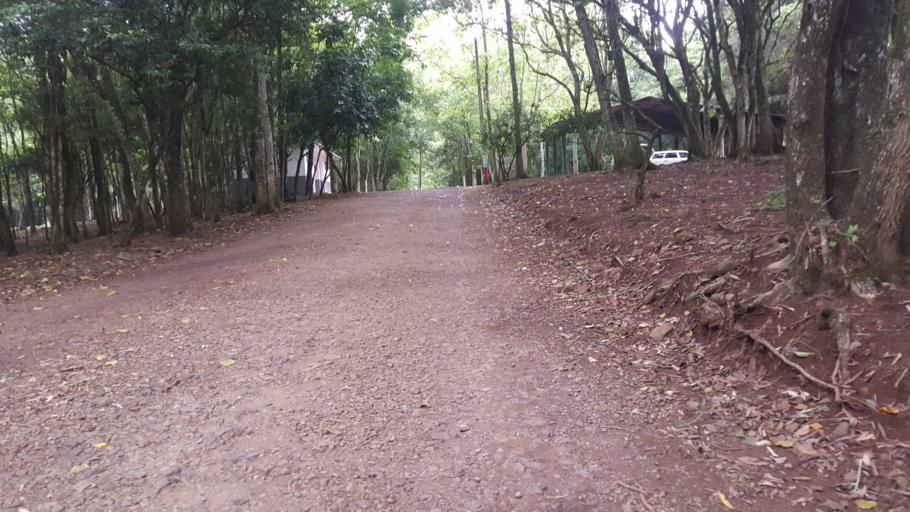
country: BR
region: Rio Grande do Sul
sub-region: Frederico Westphalen
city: Frederico Westphalen
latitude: -27.0889
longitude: -53.3775
